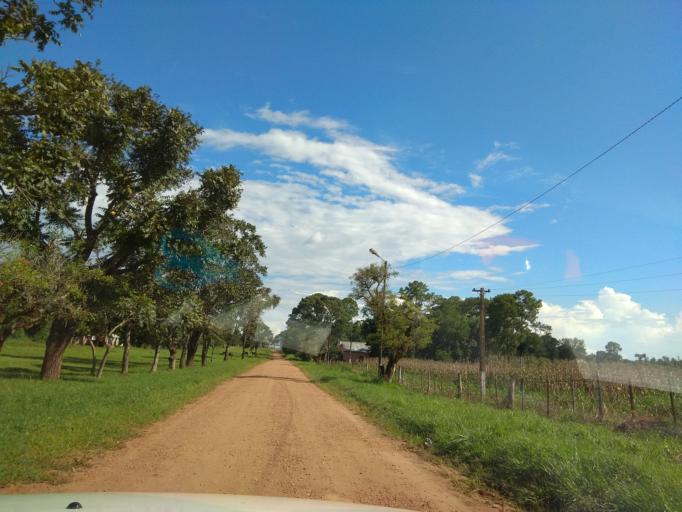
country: AR
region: Misiones
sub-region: Departamento de Candelaria
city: Candelaria
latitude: -27.4560
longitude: -55.7548
